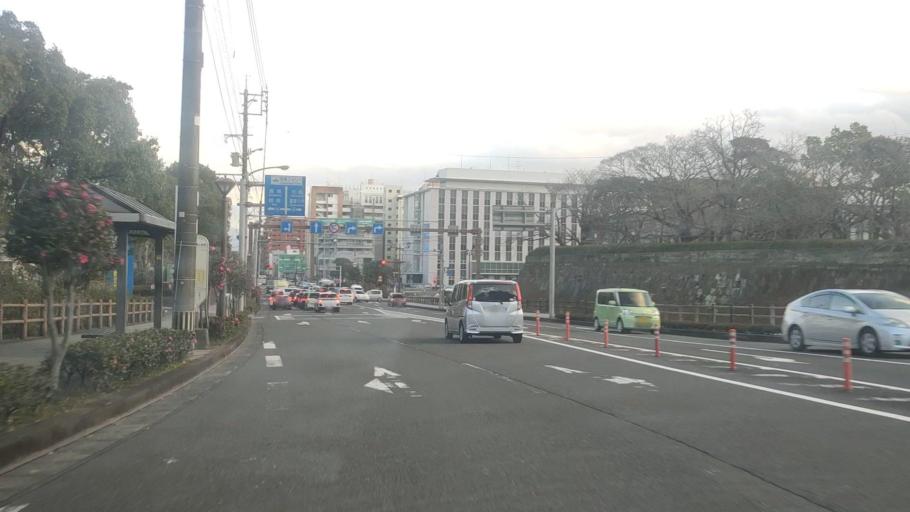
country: JP
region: Kagoshima
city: Kagoshima-shi
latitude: 31.5996
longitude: 130.5553
